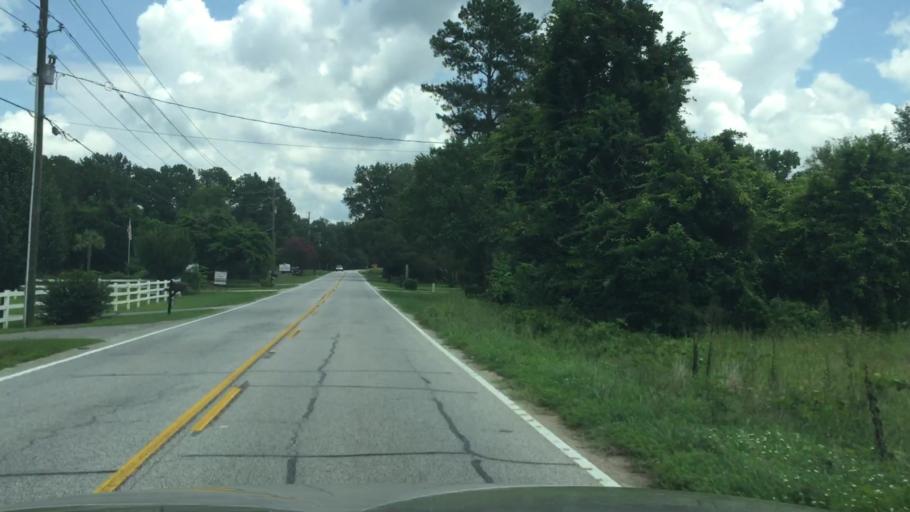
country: US
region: South Carolina
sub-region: Sumter County
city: South Sumter
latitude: 33.9120
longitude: -80.3984
